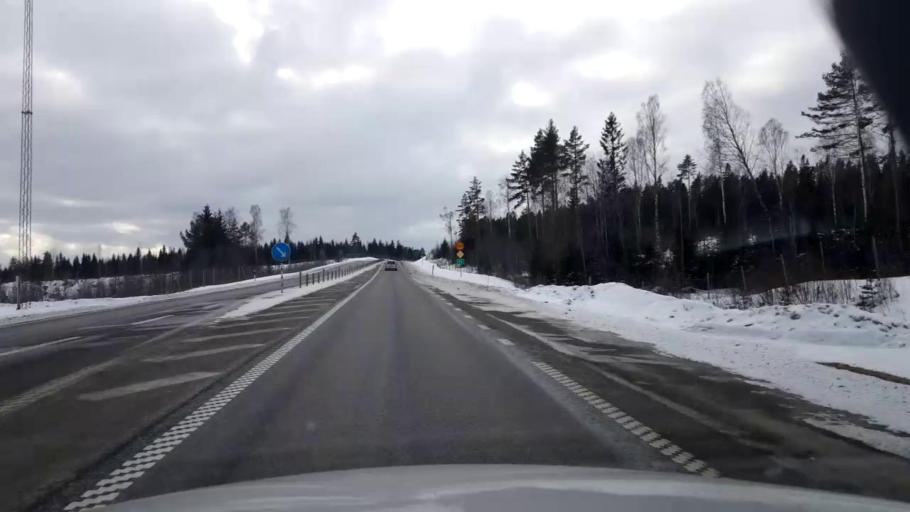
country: SE
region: Vaesternorrland
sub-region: Sundsvalls Kommun
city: Njurundabommen
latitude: 62.0948
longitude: 17.3055
